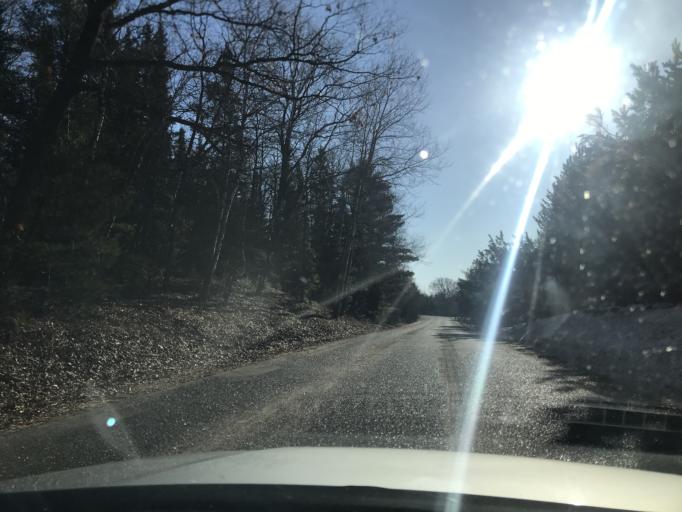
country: US
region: Wisconsin
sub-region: Marinette County
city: Niagara
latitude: 45.3681
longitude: -88.0228
